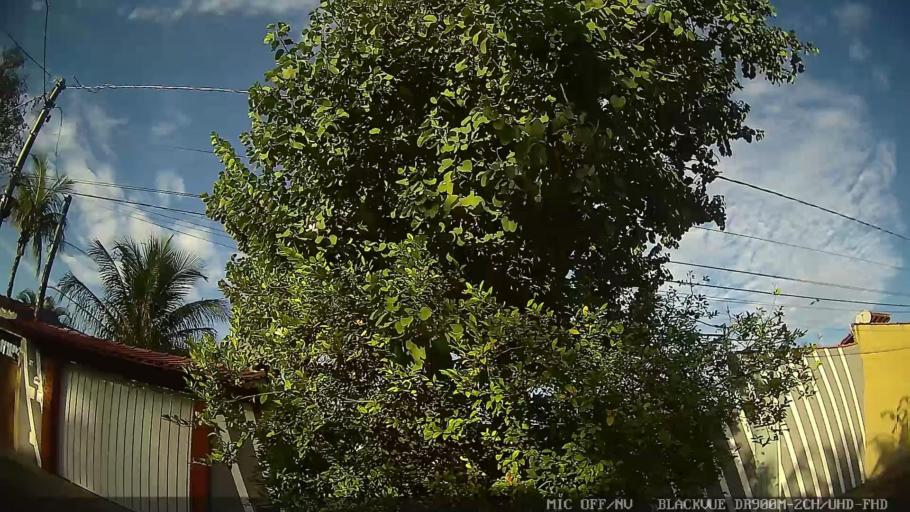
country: BR
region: Sao Paulo
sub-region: Salto
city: Salto
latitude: -23.1920
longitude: -47.2668
